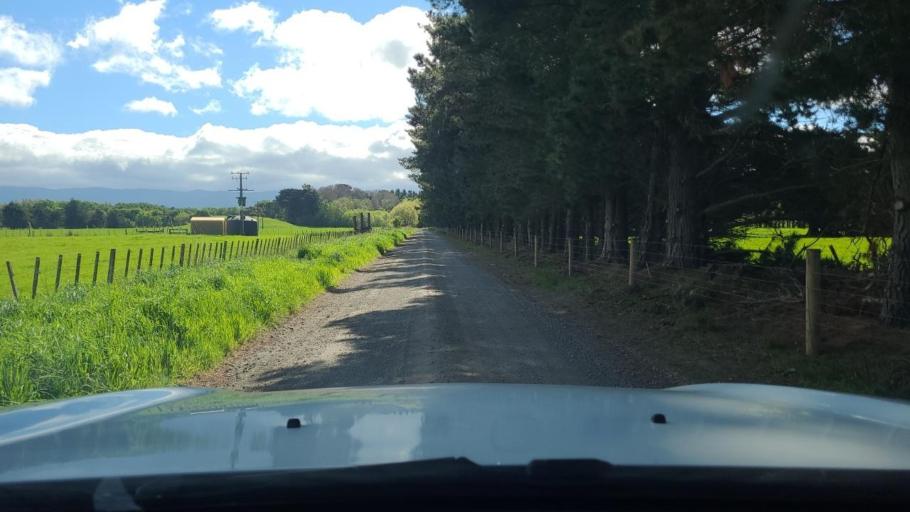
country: NZ
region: Wellington
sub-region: South Wairarapa District
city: Waipawa
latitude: -41.2256
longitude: 175.3148
